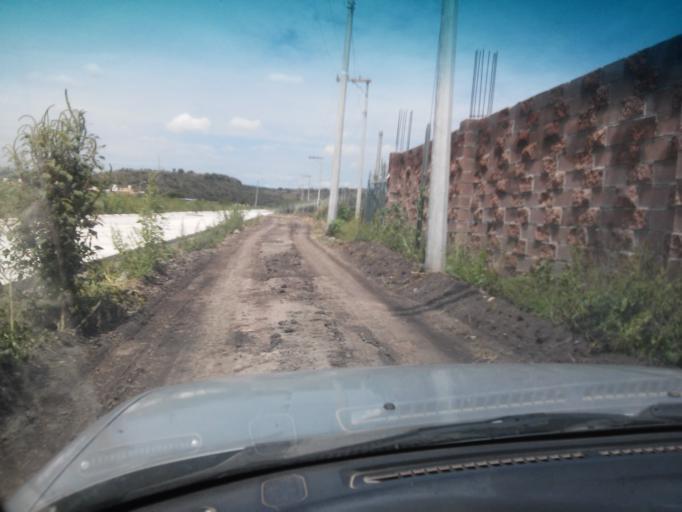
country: MX
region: Durango
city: Victoria de Durango
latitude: 23.9977
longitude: -104.7049
